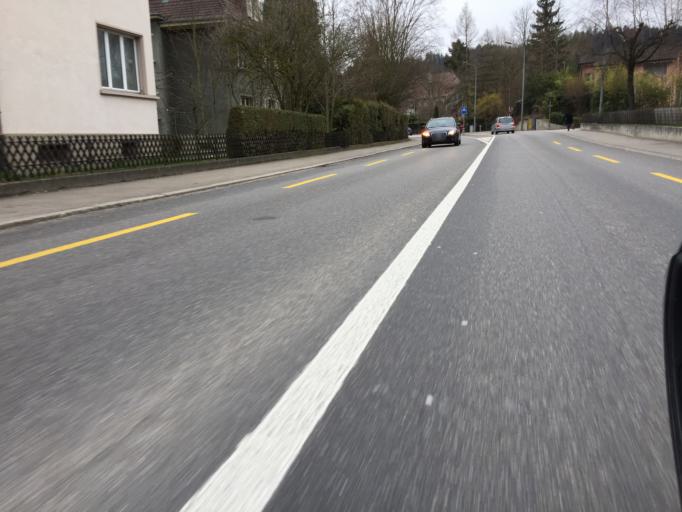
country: CH
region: Bern
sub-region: Emmental District
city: Burgdorf
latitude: 47.0513
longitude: 7.6232
